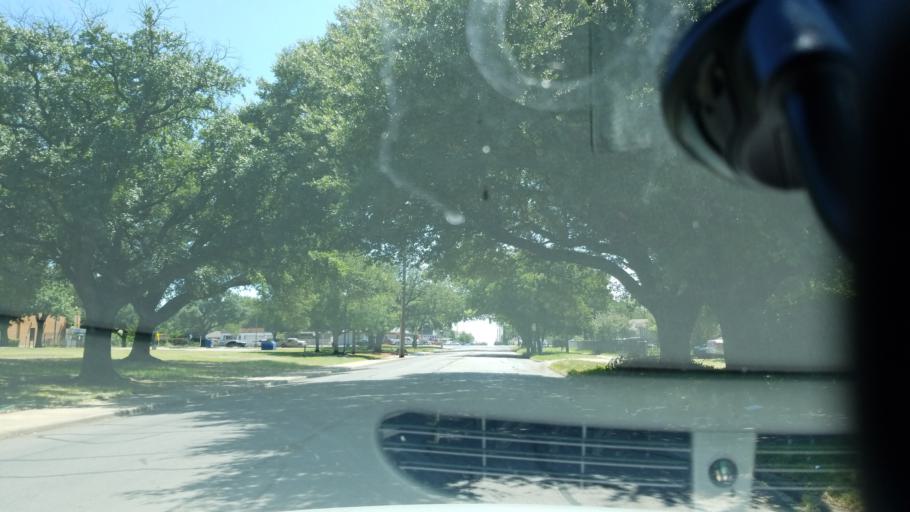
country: US
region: Texas
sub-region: Dallas County
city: Cockrell Hill
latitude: 32.7131
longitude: -96.8247
